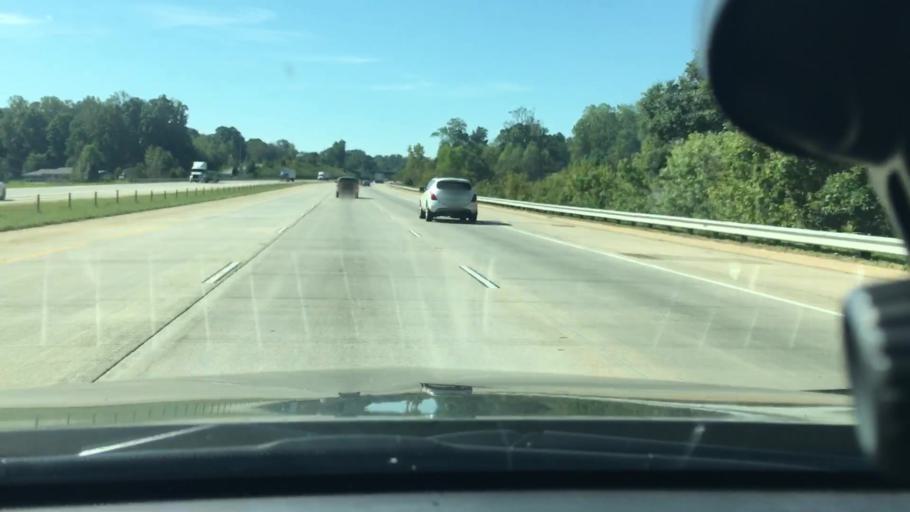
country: US
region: North Carolina
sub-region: Gaston County
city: Mount Holly
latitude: 35.3026
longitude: -80.9557
